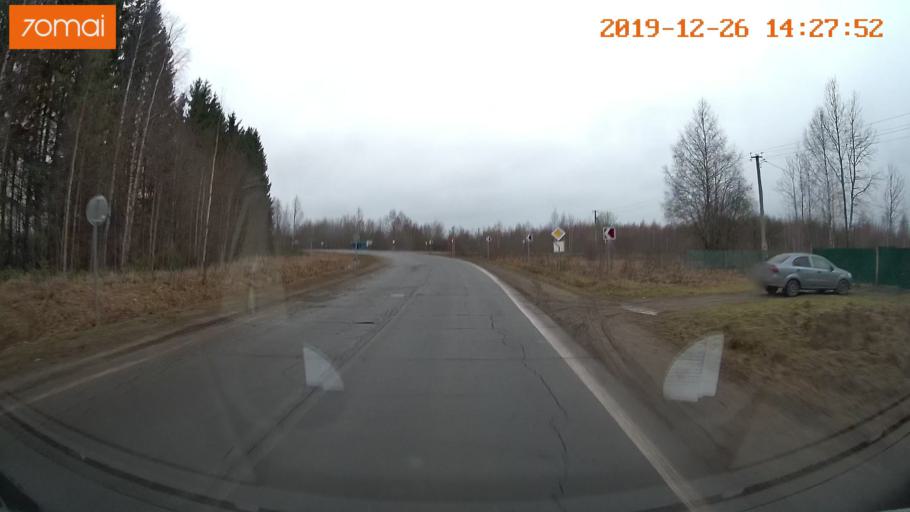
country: RU
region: Jaroslavl
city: Poshekhon'ye
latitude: 58.4812
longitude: 39.0602
